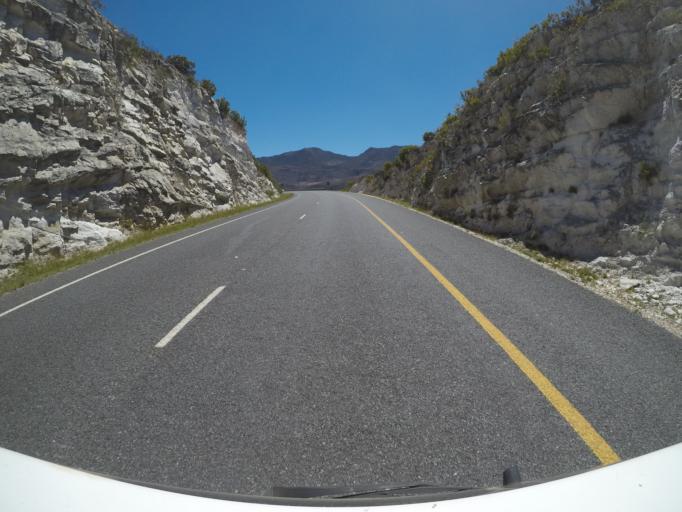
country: ZA
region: Western Cape
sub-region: Overberg District Municipality
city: Grabouw
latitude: -34.2188
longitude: 19.1739
